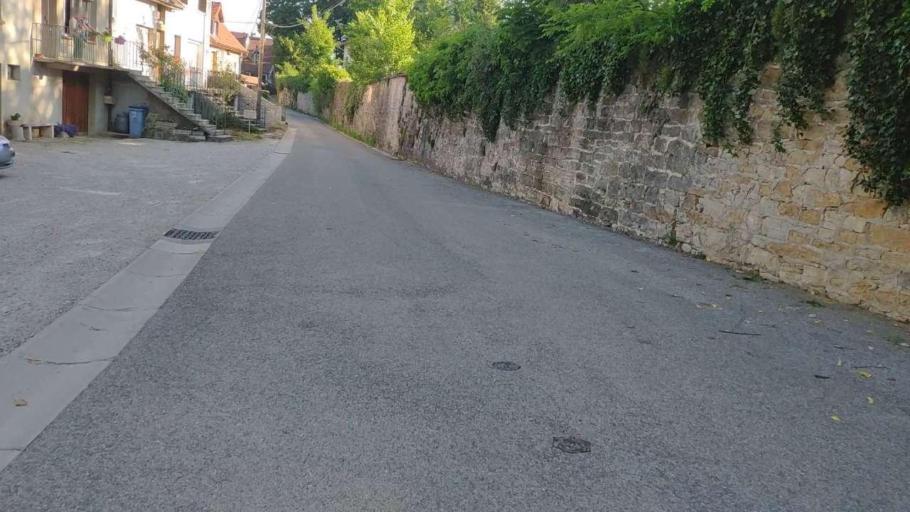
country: FR
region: Franche-Comte
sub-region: Departement du Jura
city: Perrigny
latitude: 46.7142
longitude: 5.5956
